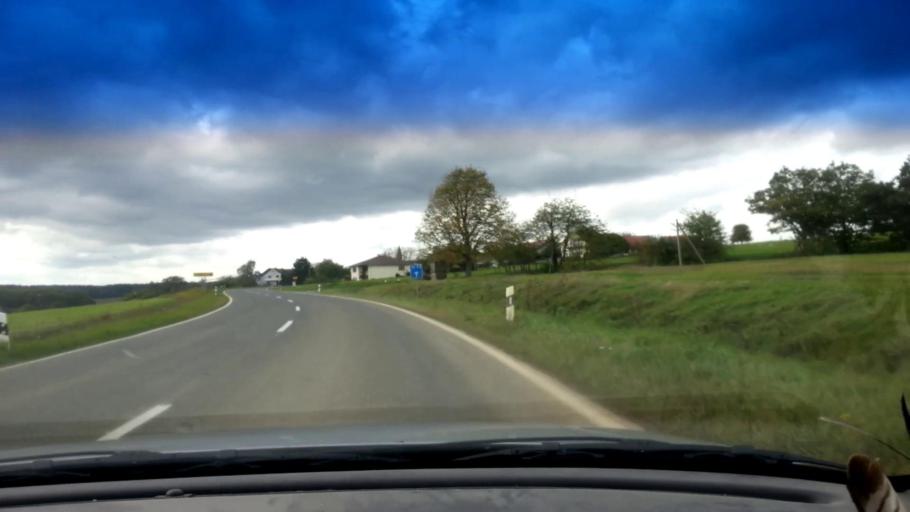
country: DE
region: Bavaria
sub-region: Upper Franconia
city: Schesslitz
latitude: 49.9955
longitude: 11.0033
